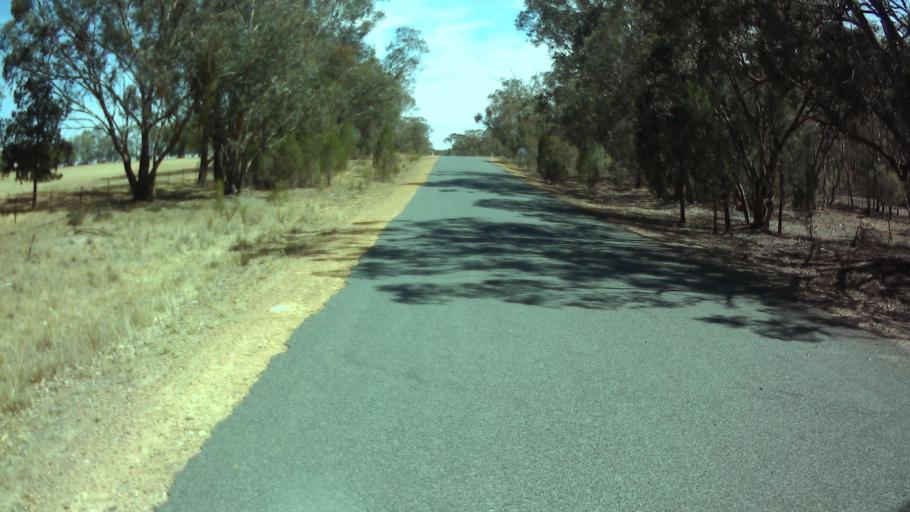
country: AU
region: New South Wales
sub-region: Weddin
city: Grenfell
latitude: -34.0032
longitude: 148.1306
